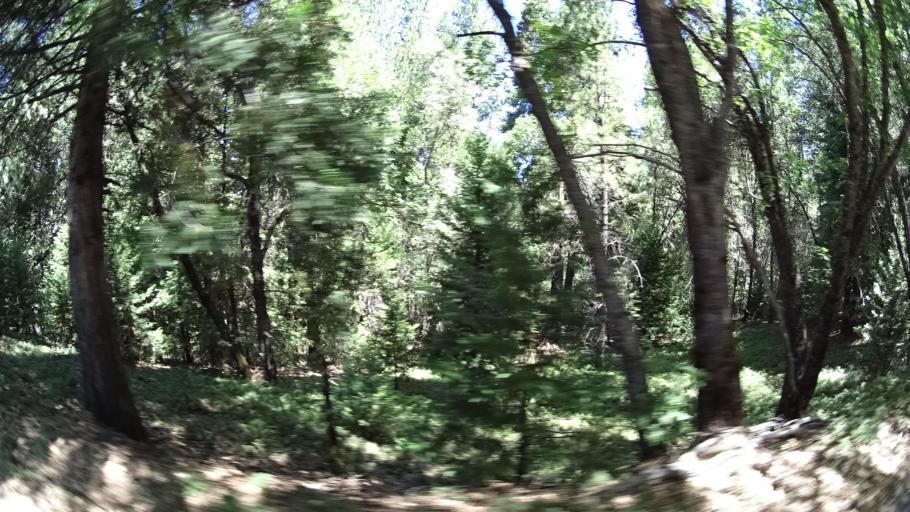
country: US
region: California
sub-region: Amador County
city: Pioneer
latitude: 38.4120
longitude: -120.5000
